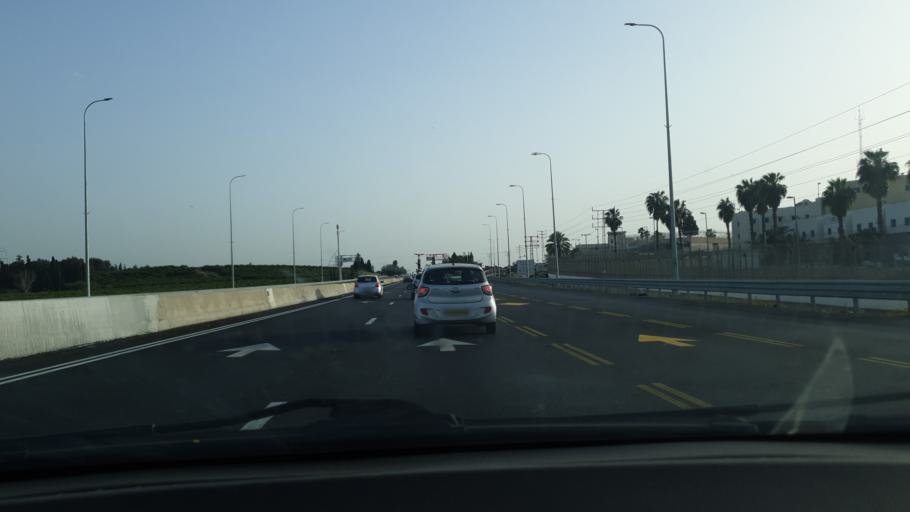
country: IL
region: Central District
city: Even Yehuda
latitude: 32.2422
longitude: 34.8873
